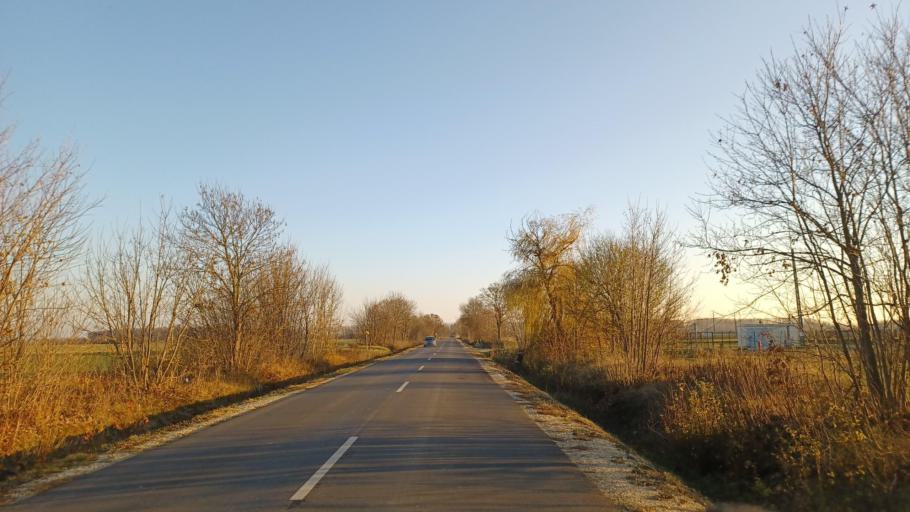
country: HU
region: Tolna
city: Fadd
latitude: 46.4926
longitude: 18.8335
